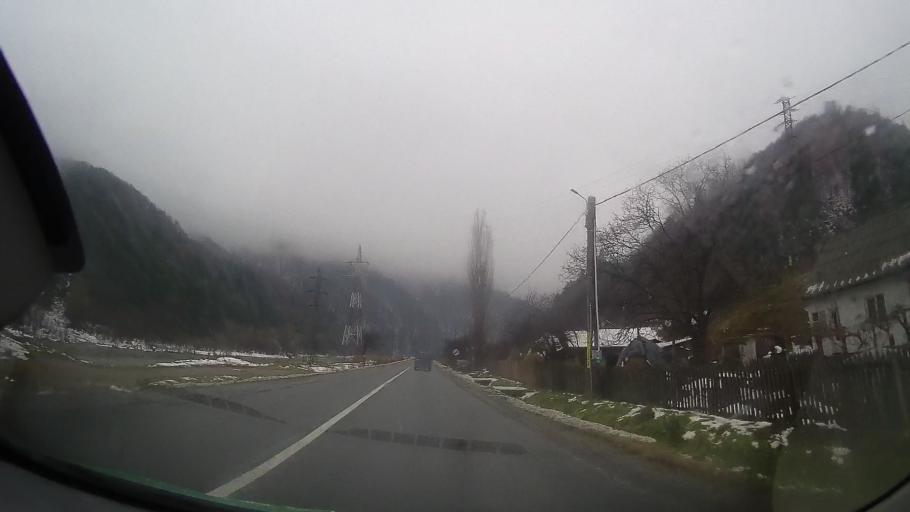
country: RO
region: Neamt
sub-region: Comuna Pangarati
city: Stejaru
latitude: 46.8935
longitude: 26.1689
